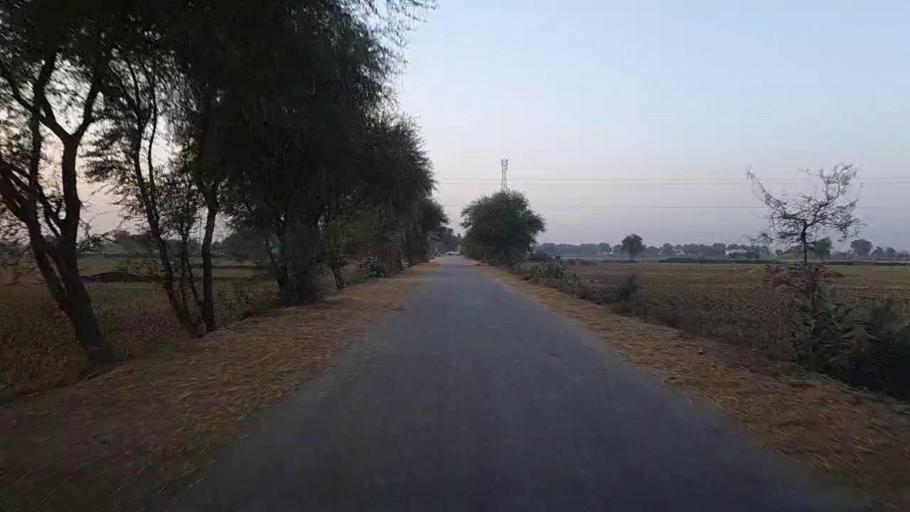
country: PK
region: Sindh
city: Kashmor
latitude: 28.4163
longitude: 69.4511
